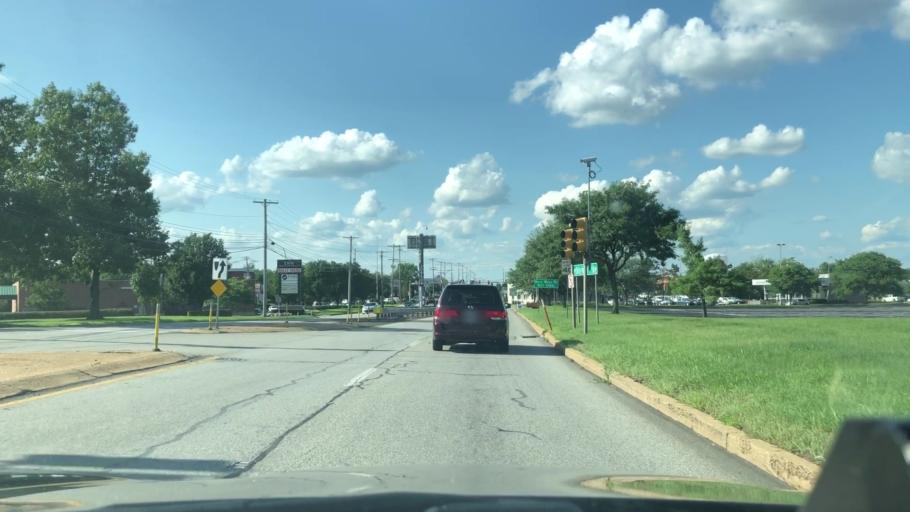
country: US
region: Pennsylvania
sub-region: Montgomery County
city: Montgomeryville
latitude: 40.2390
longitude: -75.2424
